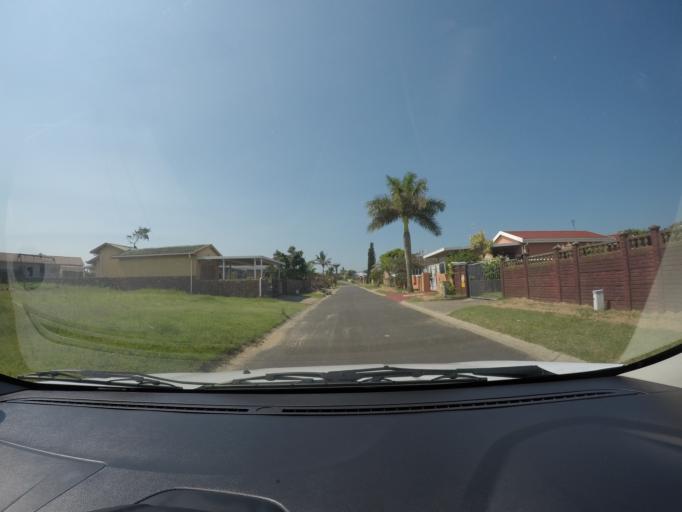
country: ZA
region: KwaZulu-Natal
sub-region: uThungulu District Municipality
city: Richards Bay
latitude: -28.7276
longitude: 32.0409
